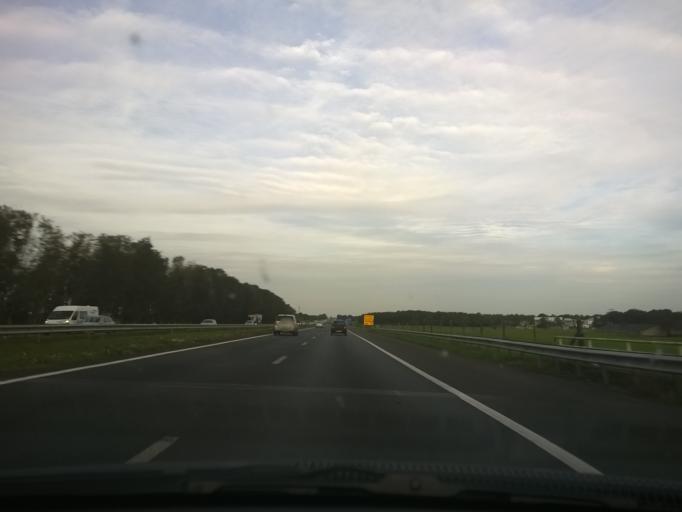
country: NL
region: Groningen
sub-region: Gemeente Grootegast
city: Grootegast
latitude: 53.1464
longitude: 6.2448
